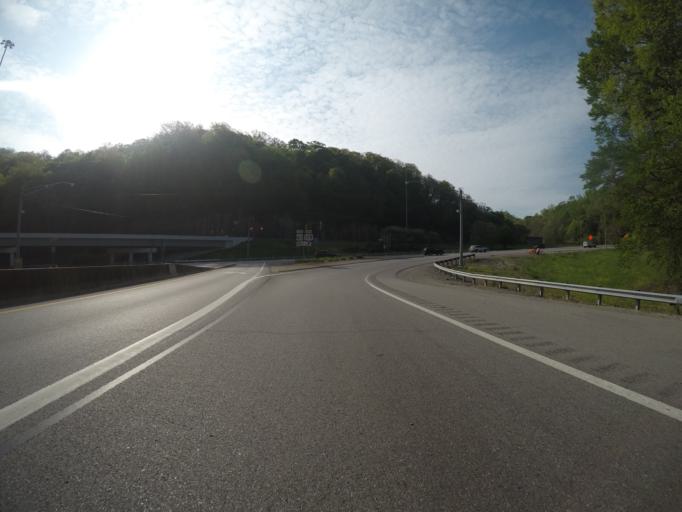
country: US
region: West Virginia
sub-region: Kanawha County
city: Charleston
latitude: 38.3490
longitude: -81.6510
